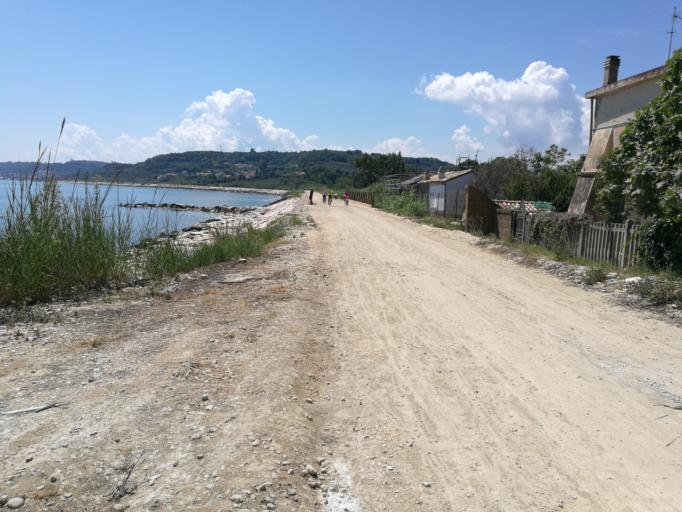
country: IT
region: Abruzzo
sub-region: Provincia di Chieti
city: Marina di San Vito
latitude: 42.3315
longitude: 14.4240
